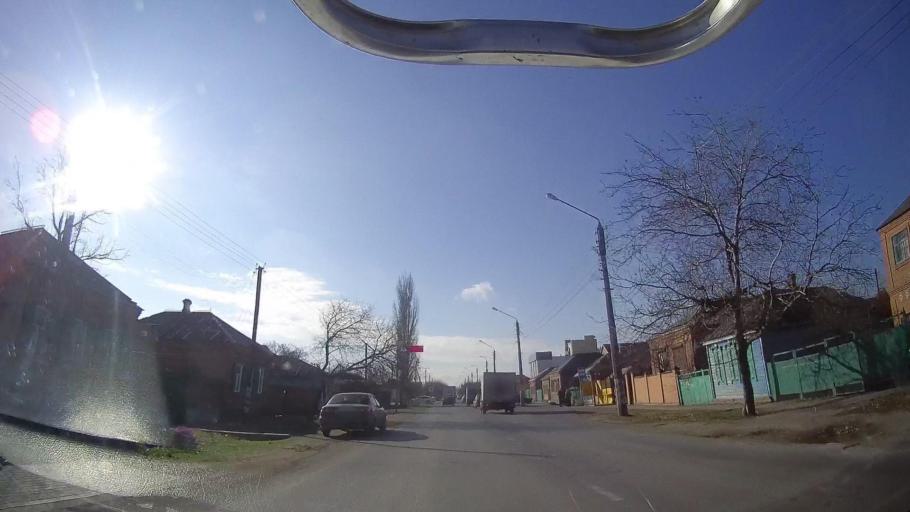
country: RU
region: Rostov
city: Bataysk
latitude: 47.1308
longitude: 39.6976
